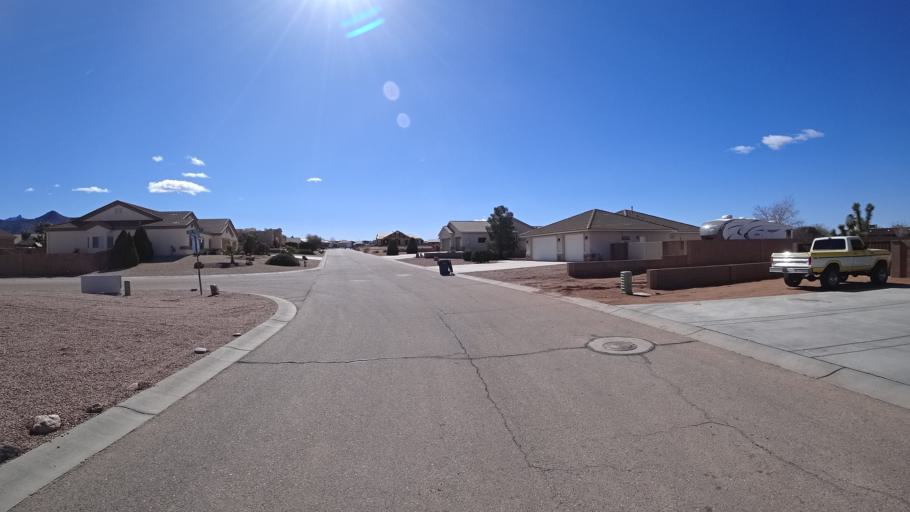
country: US
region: Arizona
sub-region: Mohave County
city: New Kingman-Butler
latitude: 35.2077
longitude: -113.9696
